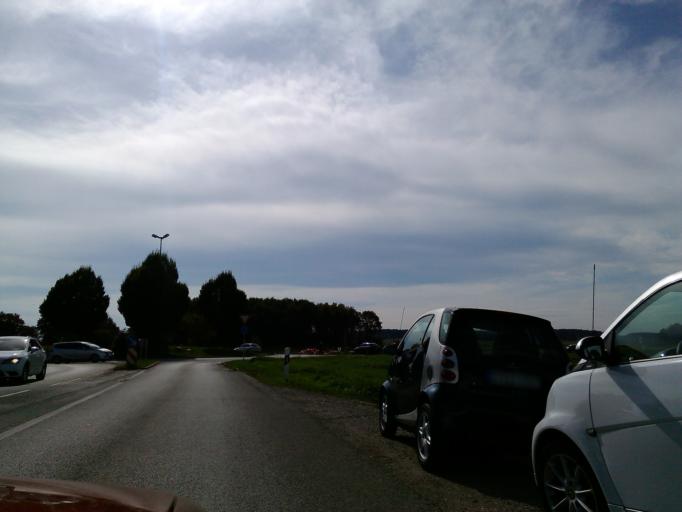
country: DE
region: Bavaria
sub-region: Upper Bavaria
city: Puchheim
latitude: 48.1580
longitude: 11.3339
